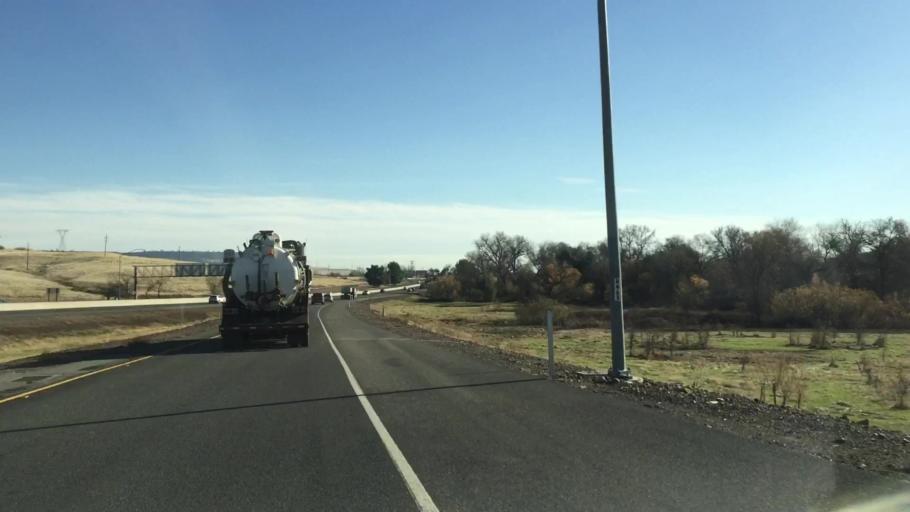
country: US
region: California
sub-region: Butte County
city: Thermalito
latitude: 39.5796
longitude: -121.6212
